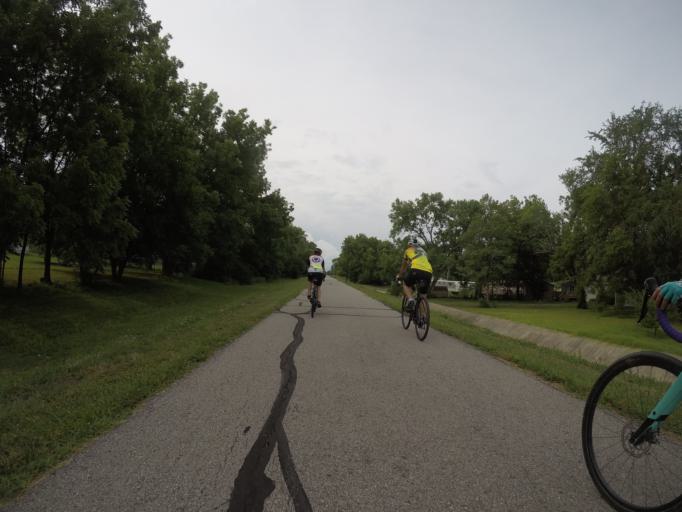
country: US
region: Kansas
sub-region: Franklin County
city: Ottawa
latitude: 38.6074
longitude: -95.2701
